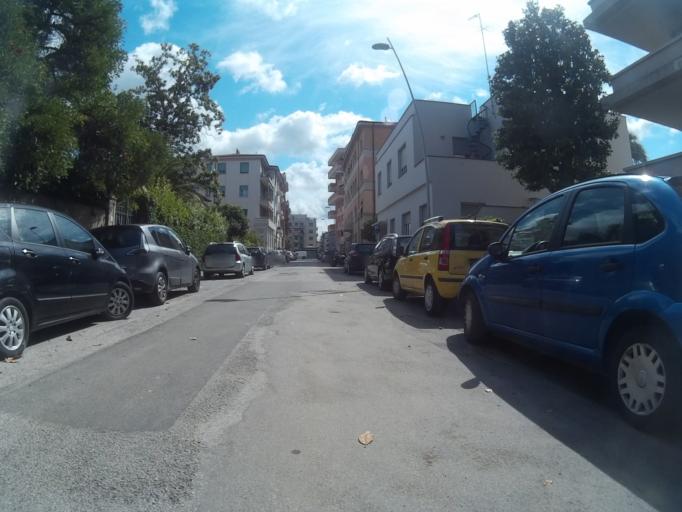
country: IT
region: Tuscany
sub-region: Provincia di Livorno
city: Livorno
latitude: 43.5382
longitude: 10.3164
